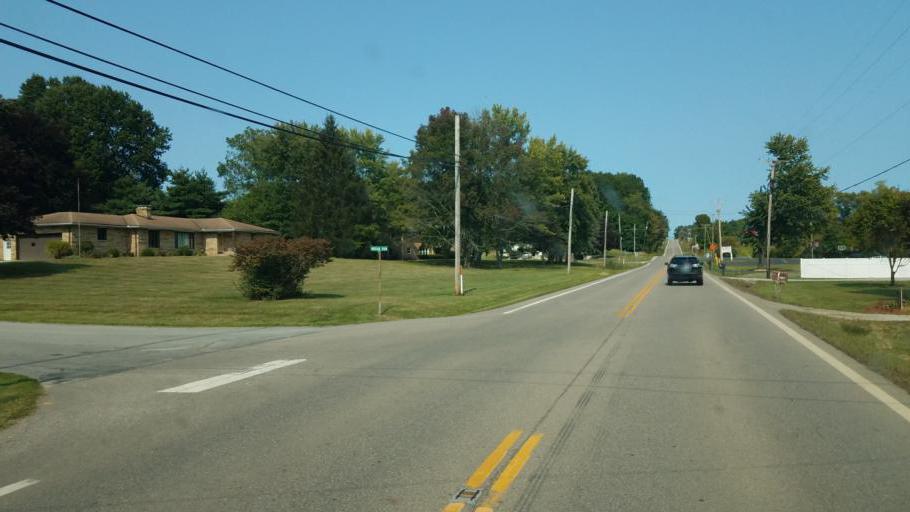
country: US
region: Ohio
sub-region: Wayne County
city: Wooster
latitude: 40.7615
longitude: -81.9868
